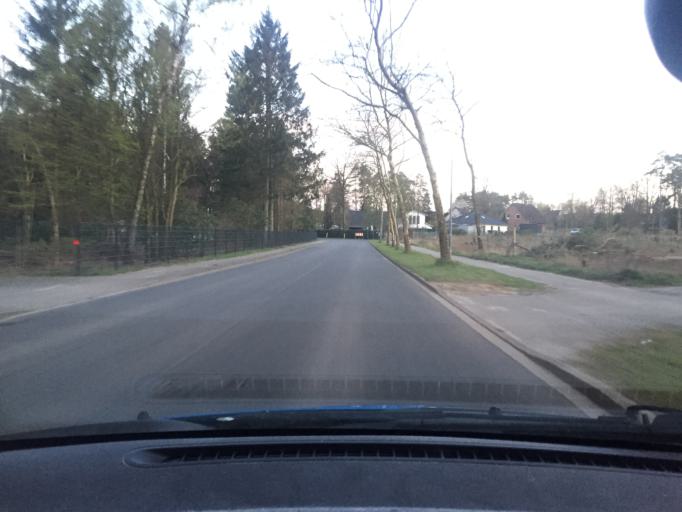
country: DE
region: Lower Saxony
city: Buchholz in der Nordheide
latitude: 53.3100
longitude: 9.8655
